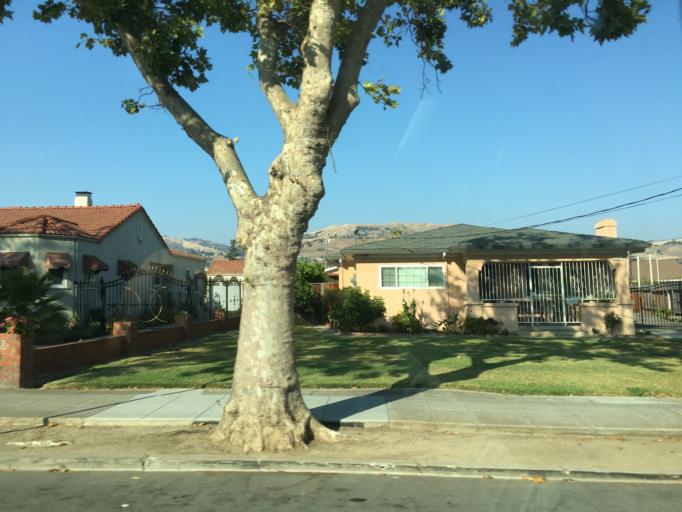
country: US
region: California
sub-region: Santa Clara County
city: Alum Rock
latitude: 37.3691
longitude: -121.8309
